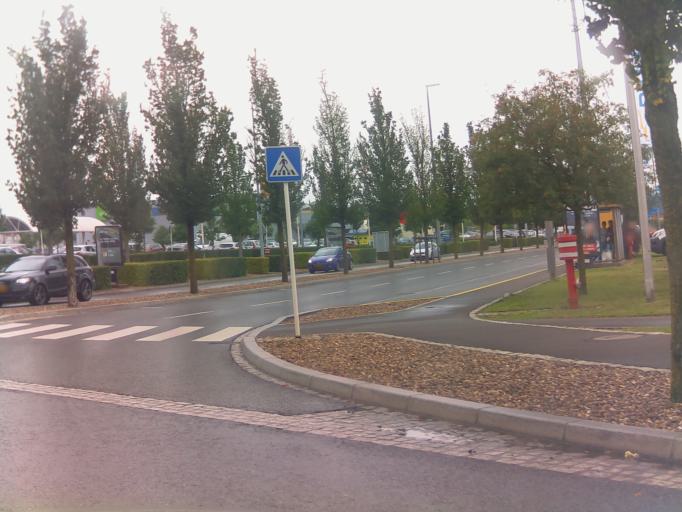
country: LU
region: Luxembourg
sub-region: Canton d'Esch-sur-Alzette
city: Schifflange
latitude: 49.5217
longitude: 6.0101
